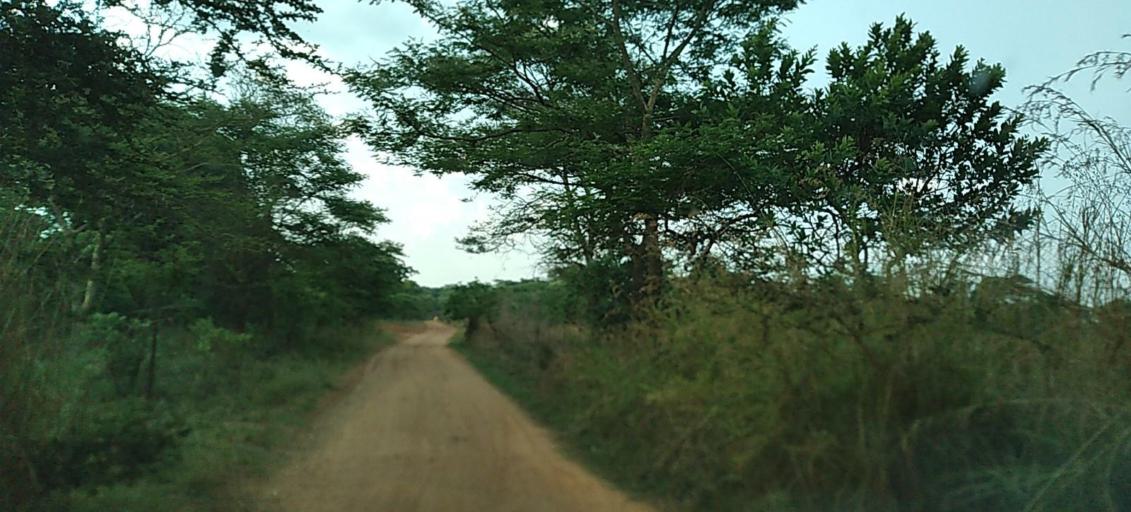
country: ZM
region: Copperbelt
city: Mpongwe
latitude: -13.5106
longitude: 28.0941
